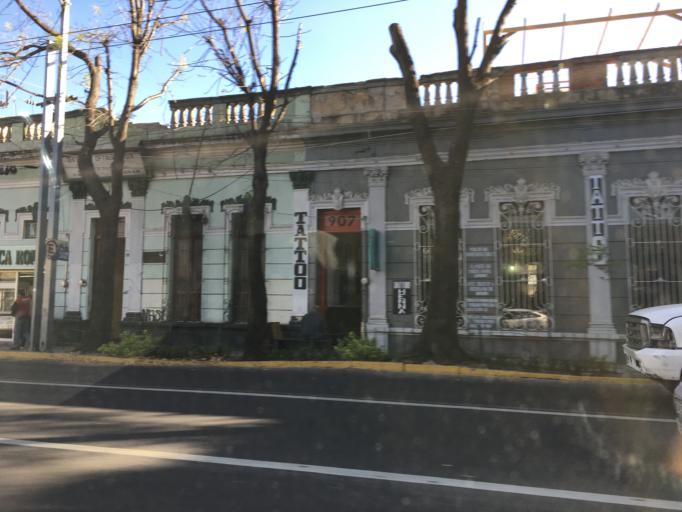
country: MX
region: Jalisco
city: Guadalajara
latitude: 20.6772
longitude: -103.3577
